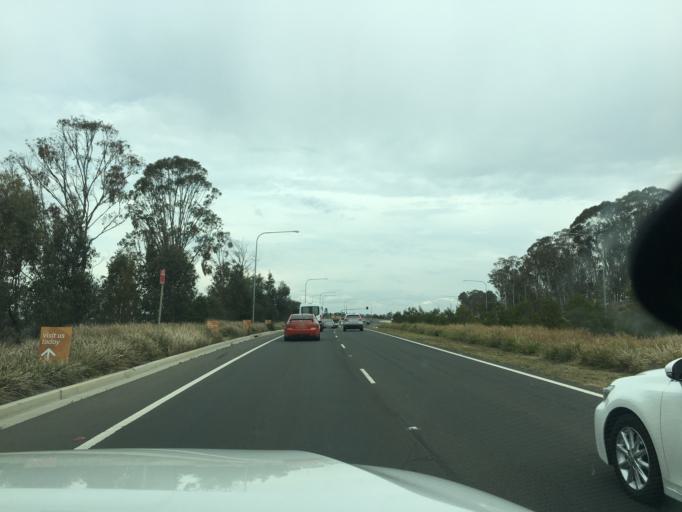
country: AU
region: New South Wales
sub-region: Campbelltown Municipality
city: Denham Court
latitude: -33.9735
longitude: 150.8117
